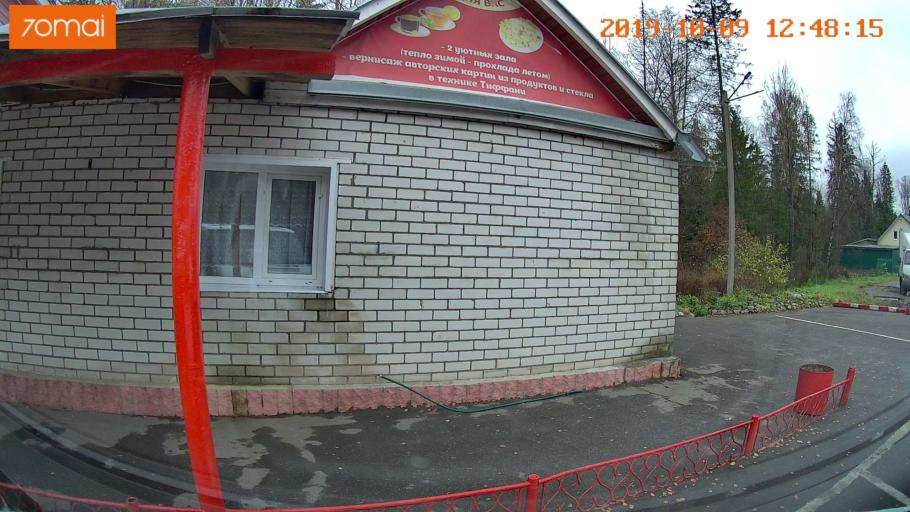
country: RU
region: Jaroslavl
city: Prechistoye
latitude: 58.4358
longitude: 40.3214
